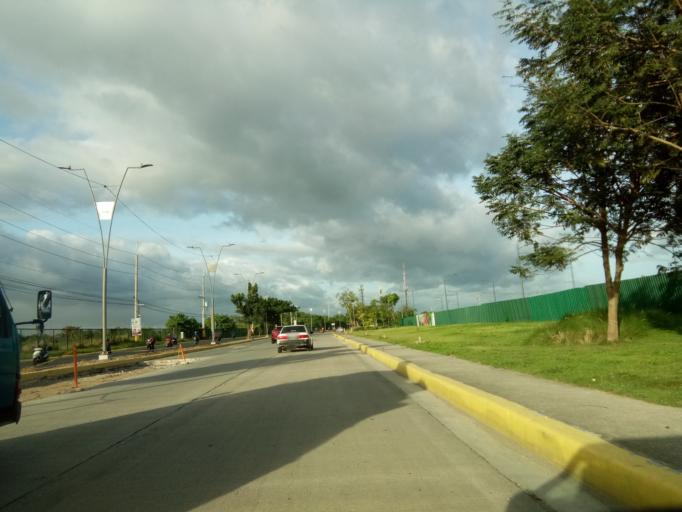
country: PH
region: Calabarzon
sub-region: Province of Cavite
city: Imus
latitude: 14.3846
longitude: 120.9596
